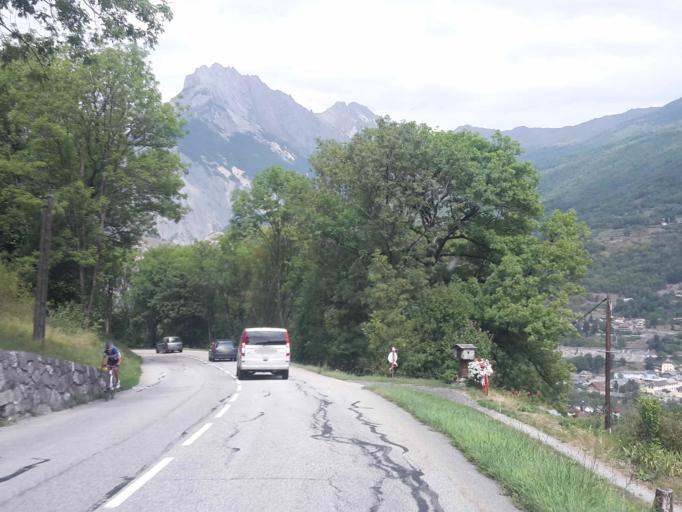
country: FR
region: Rhone-Alpes
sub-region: Departement de la Savoie
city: Saint-Michel-de-Maurienne
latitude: 45.2088
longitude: 6.4689
